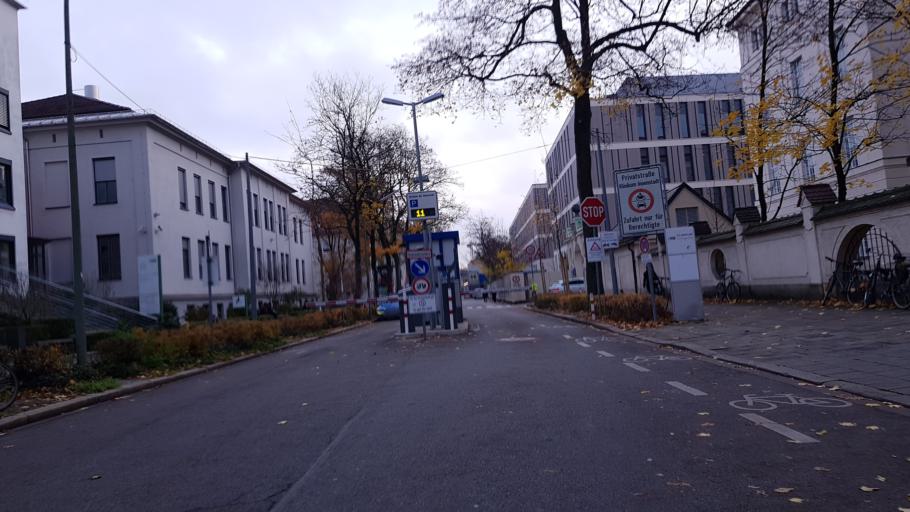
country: DE
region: Bavaria
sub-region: Upper Bavaria
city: Munich
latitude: 48.1329
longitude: 11.5594
